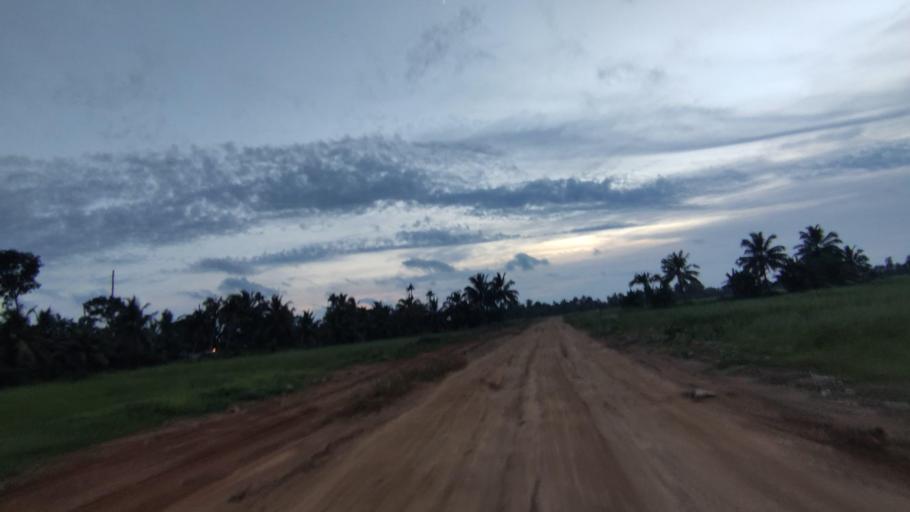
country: IN
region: Kerala
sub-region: Kottayam
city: Kottayam
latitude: 9.6452
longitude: 76.4571
